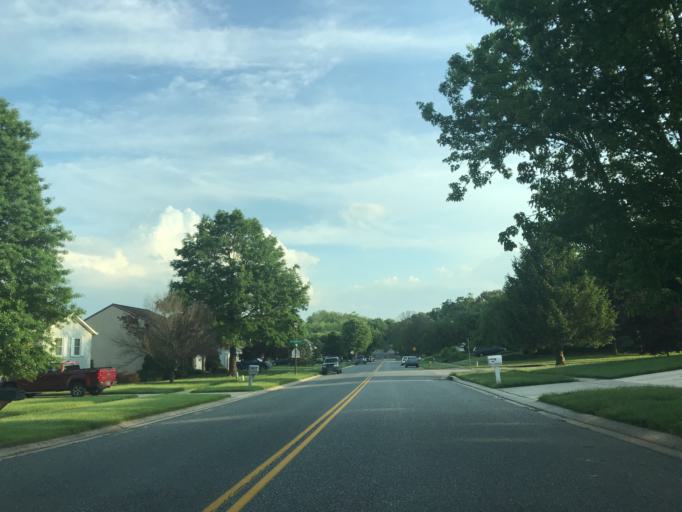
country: US
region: Maryland
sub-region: Harford County
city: South Bel Air
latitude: 39.5461
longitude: -76.3353
